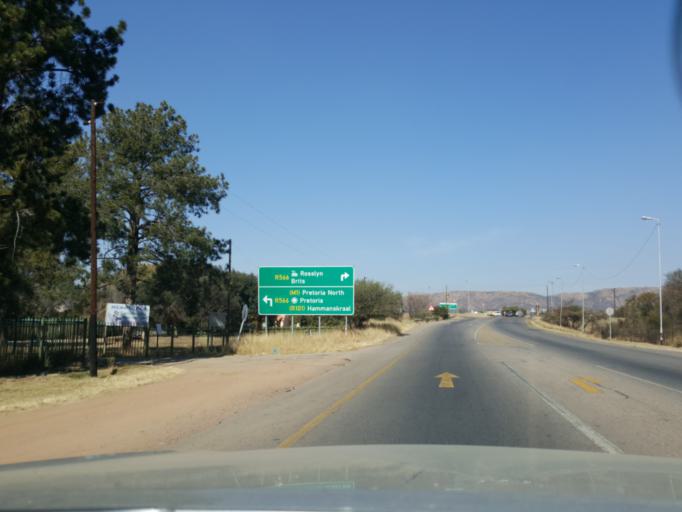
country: ZA
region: Gauteng
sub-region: City of Tshwane Metropolitan Municipality
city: Pretoria
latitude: -25.6549
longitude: 28.1824
